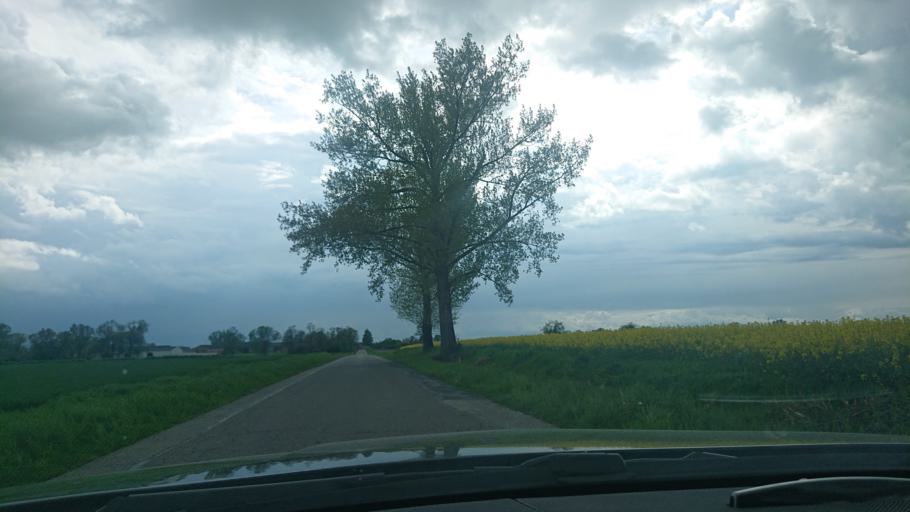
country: PL
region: Greater Poland Voivodeship
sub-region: Powiat gnieznienski
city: Niechanowo
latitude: 52.4743
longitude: 17.6347
